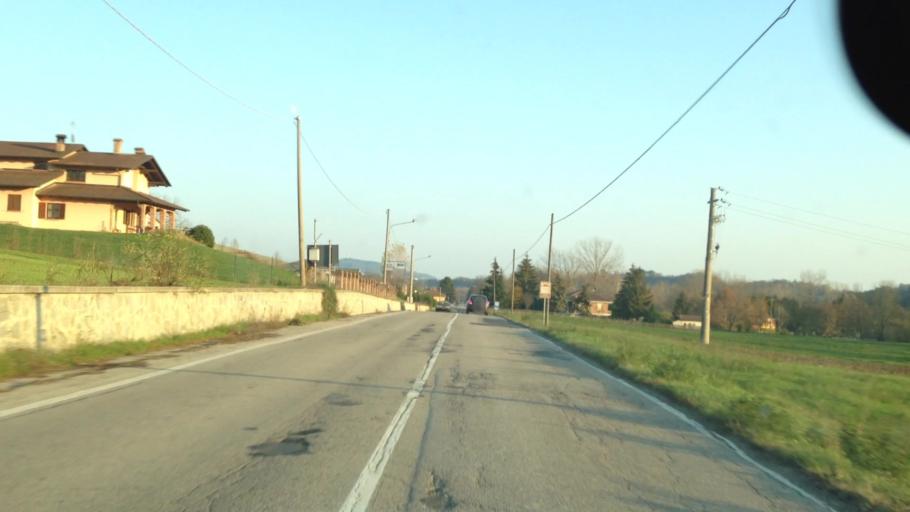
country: IT
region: Piedmont
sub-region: Provincia di Asti
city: Robella
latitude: 45.0916
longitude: 8.0929
